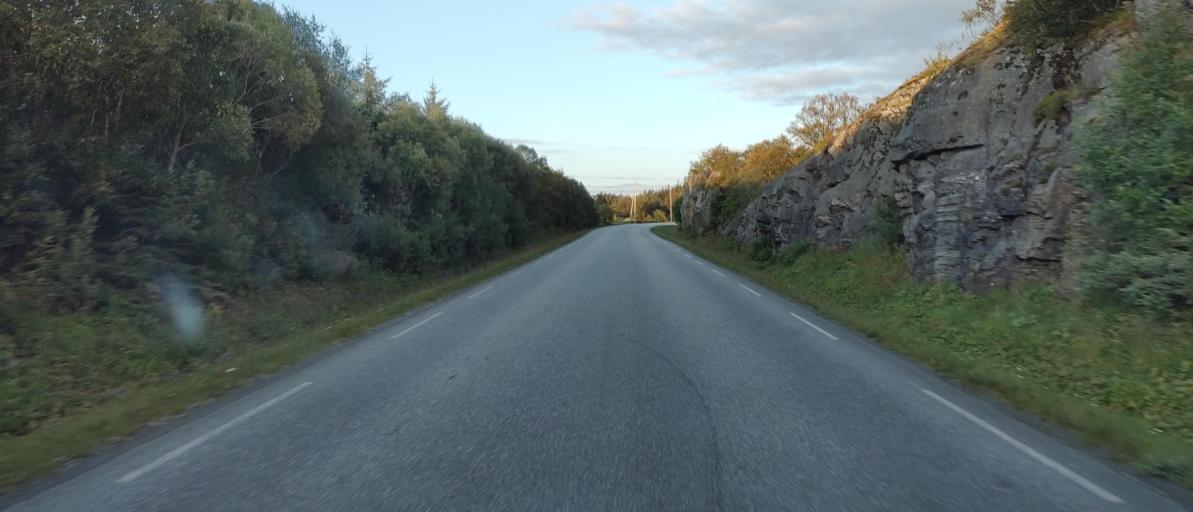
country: NO
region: More og Romsdal
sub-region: Fraena
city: Elnesvagen
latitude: 62.9911
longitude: 7.1875
